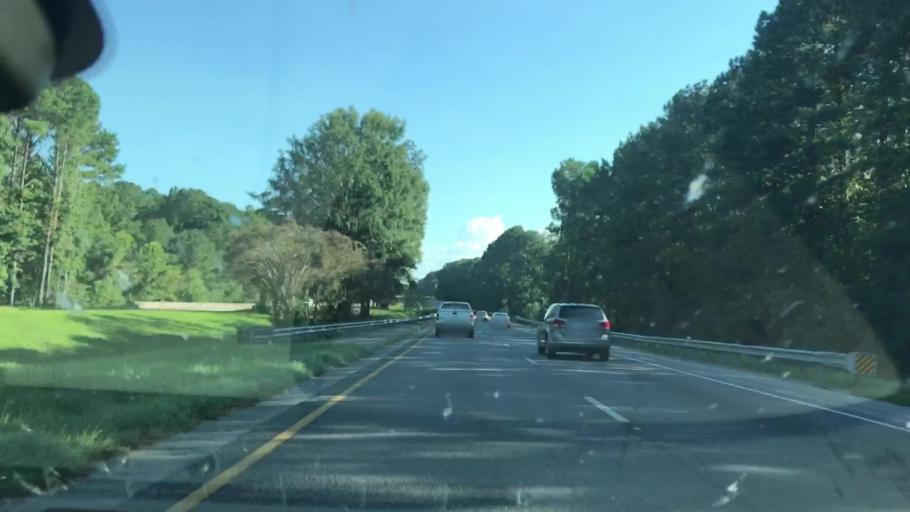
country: US
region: Georgia
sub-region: Harris County
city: Hamilton
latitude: 32.7981
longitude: -85.0216
